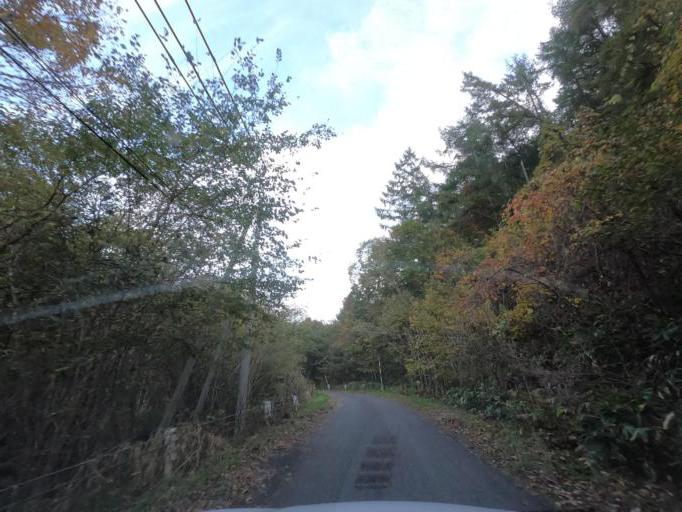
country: JP
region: Hokkaido
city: Obihiro
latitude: 42.5878
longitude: 143.3094
